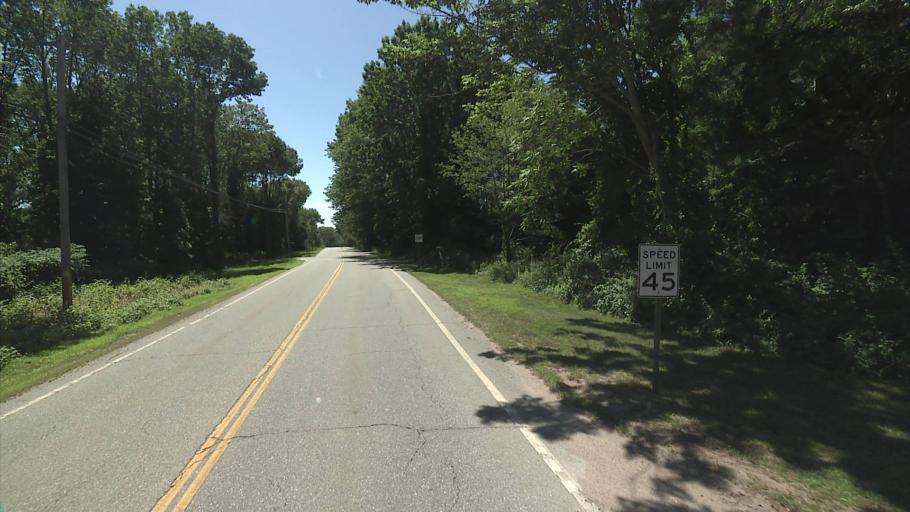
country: US
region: Connecticut
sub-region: Windham County
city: Willimantic
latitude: 41.6770
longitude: -72.2334
